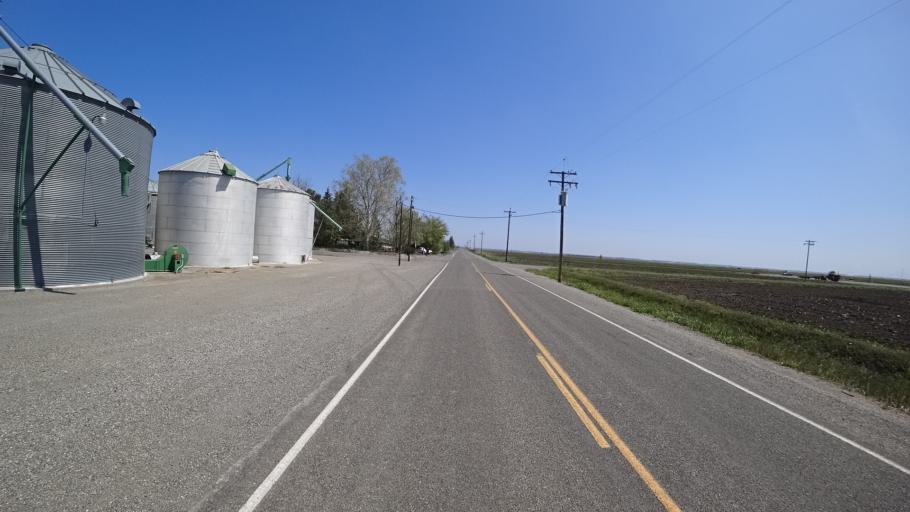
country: US
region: California
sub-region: Glenn County
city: Willows
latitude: 39.5582
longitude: -122.0846
